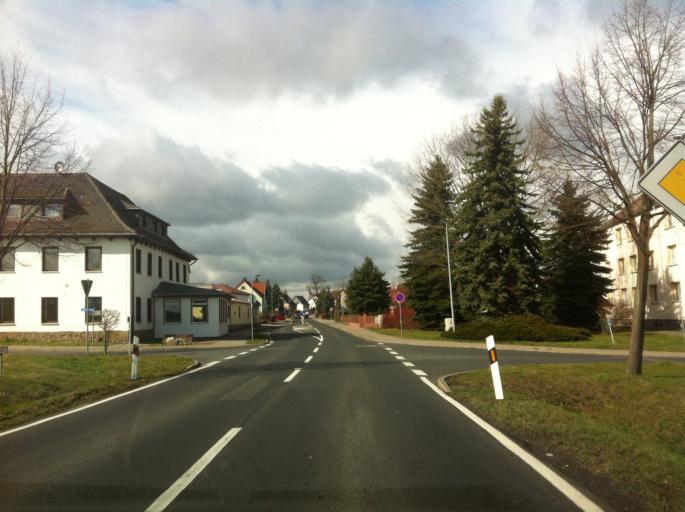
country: DE
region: Saxony
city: Trebsen
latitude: 51.3238
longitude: 12.7364
